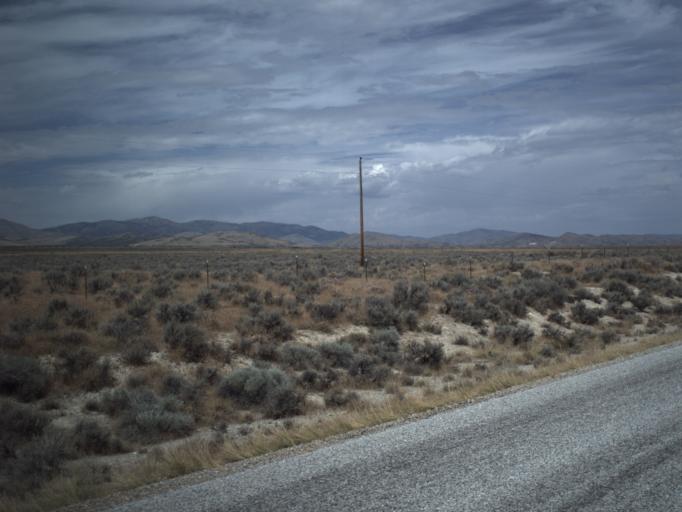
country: US
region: Utah
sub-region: Tooele County
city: Wendover
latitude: 41.5274
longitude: -113.5950
